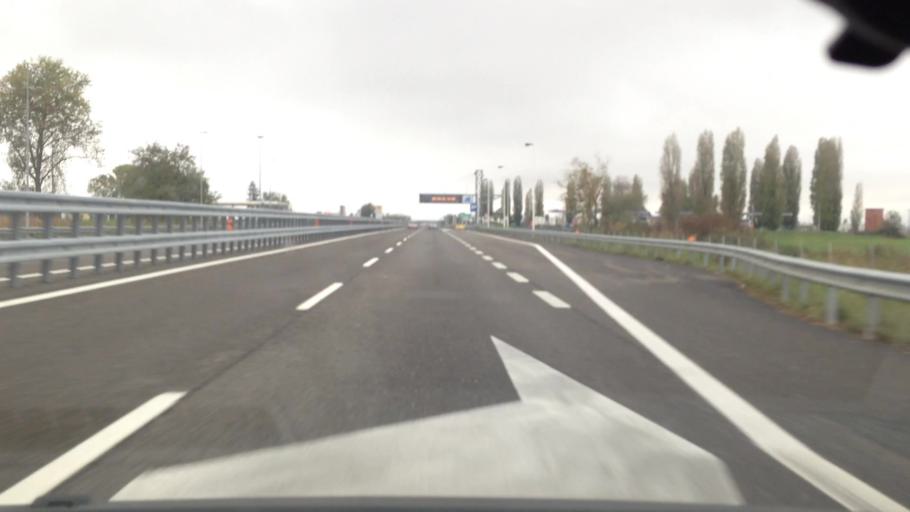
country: IT
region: Piedmont
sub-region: Provincia di Asti
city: San Paolo Solbrito
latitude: 44.9495
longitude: 7.9554
